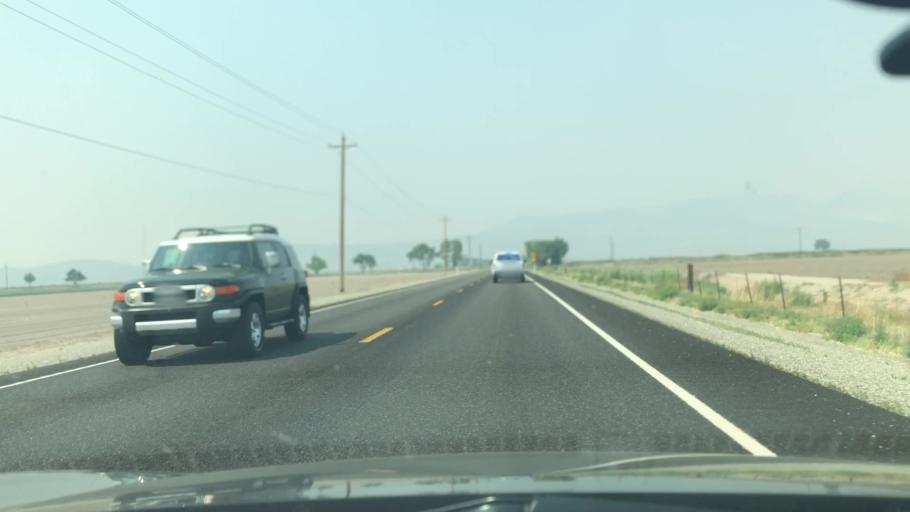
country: US
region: Nevada
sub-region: Lyon County
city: Yerington
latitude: 39.1251
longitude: -119.1810
